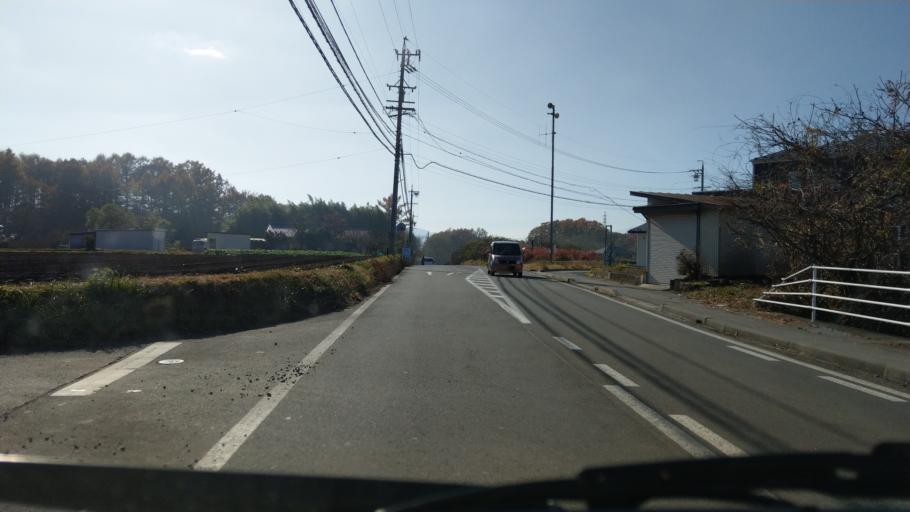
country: JP
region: Nagano
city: Komoro
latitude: 36.2980
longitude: 138.4855
